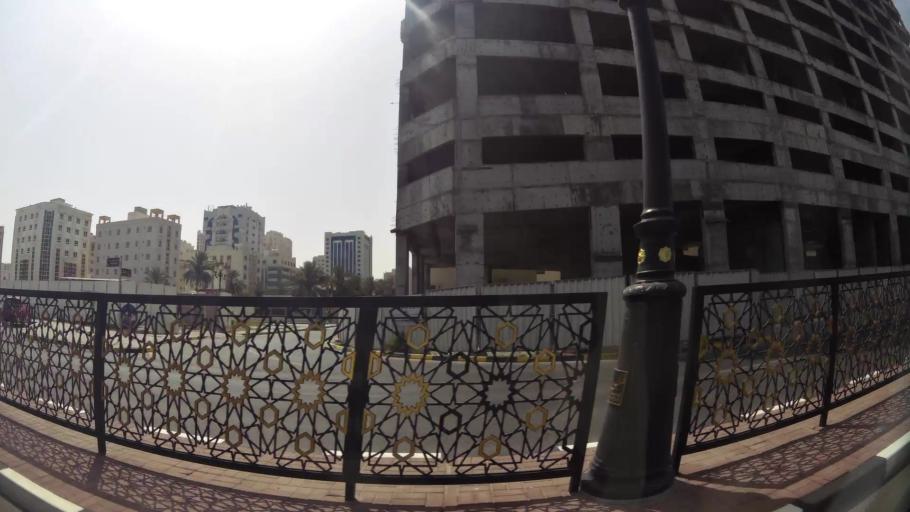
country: AE
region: Ash Shariqah
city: Sharjah
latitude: 25.3668
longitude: 55.3895
